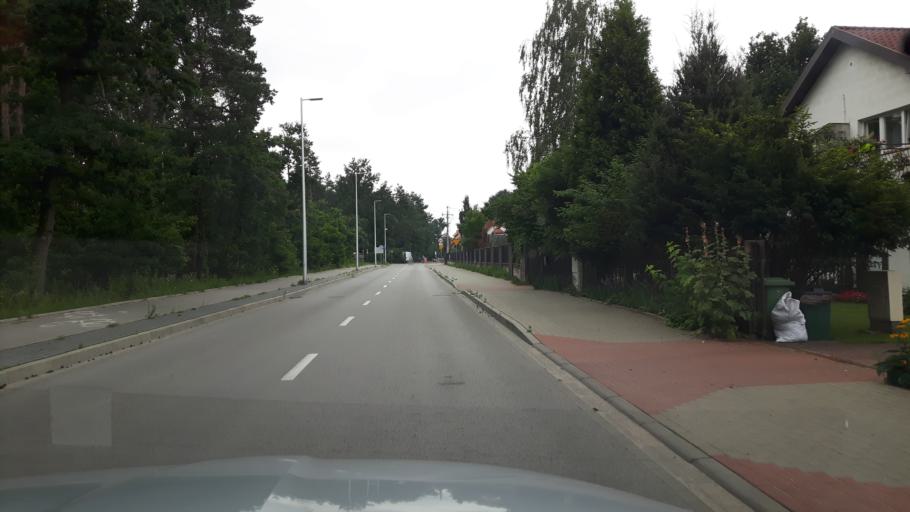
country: PL
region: Masovian Voivodeship
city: Zielonka
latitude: 52.2930
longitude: 21.1630
